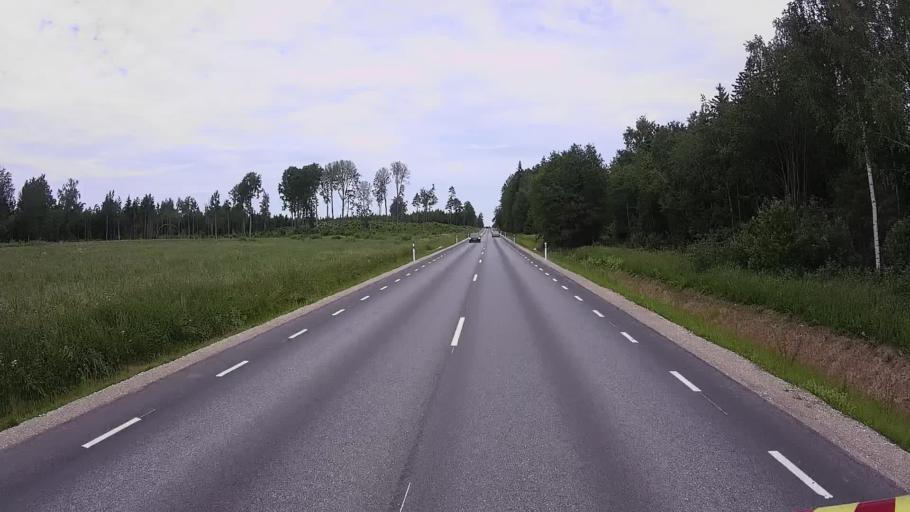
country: EE
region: Viljandimaa
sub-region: Viljandi linn
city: Viljandi
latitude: 58.2536
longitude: 25.5900
